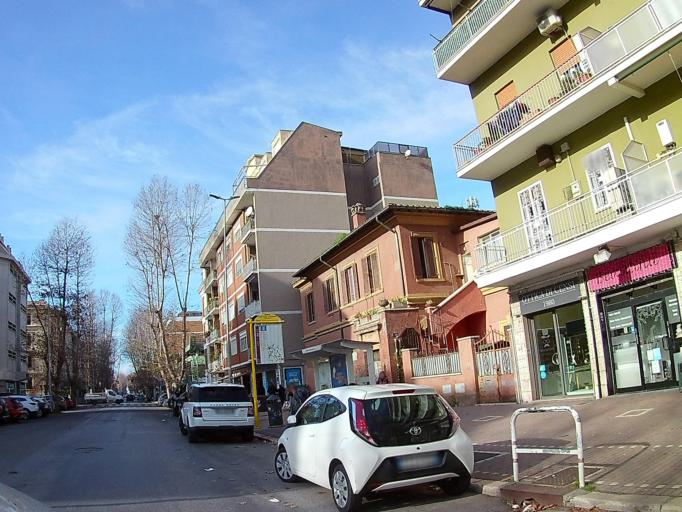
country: IT
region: Latium
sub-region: Citta metropolitana di Roma Capitale
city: Lido di Ostia
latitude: 41.7325
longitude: 12.2761
